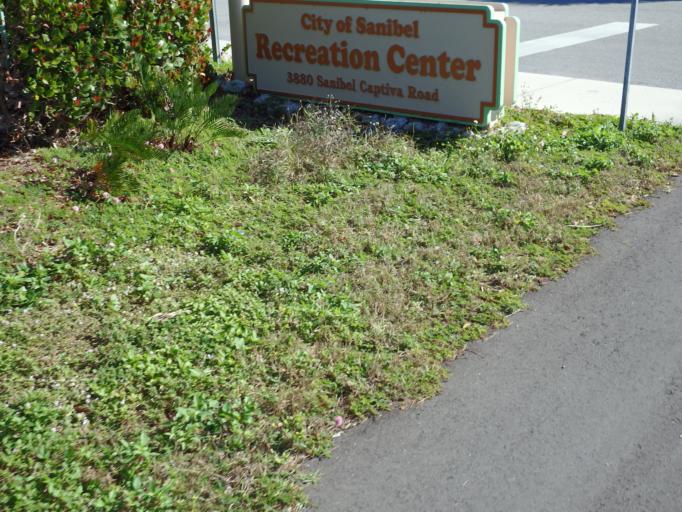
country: US
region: Florida
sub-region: Lee County
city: Saint James City
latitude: 26.4468
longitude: -82.1173
